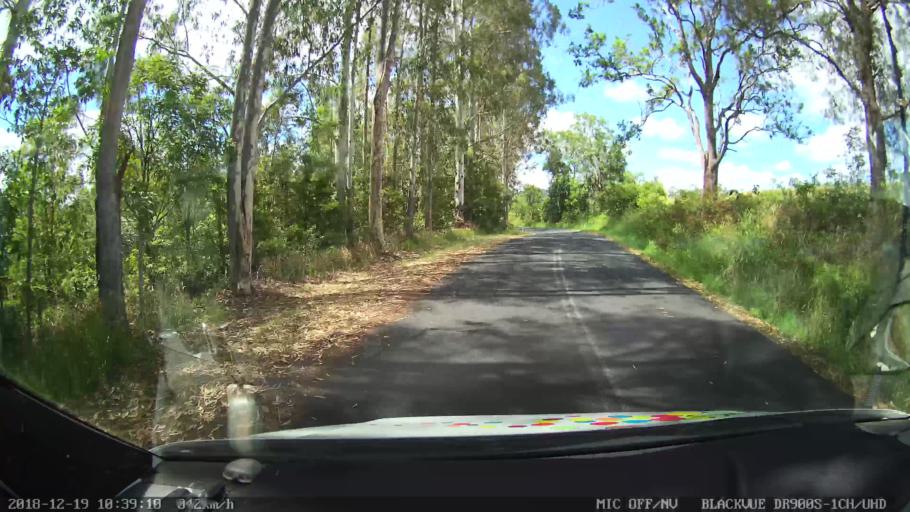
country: AU
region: New South Wales
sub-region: Lismore Municipality
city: Nimbin
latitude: -28.5789
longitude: 153.1545
